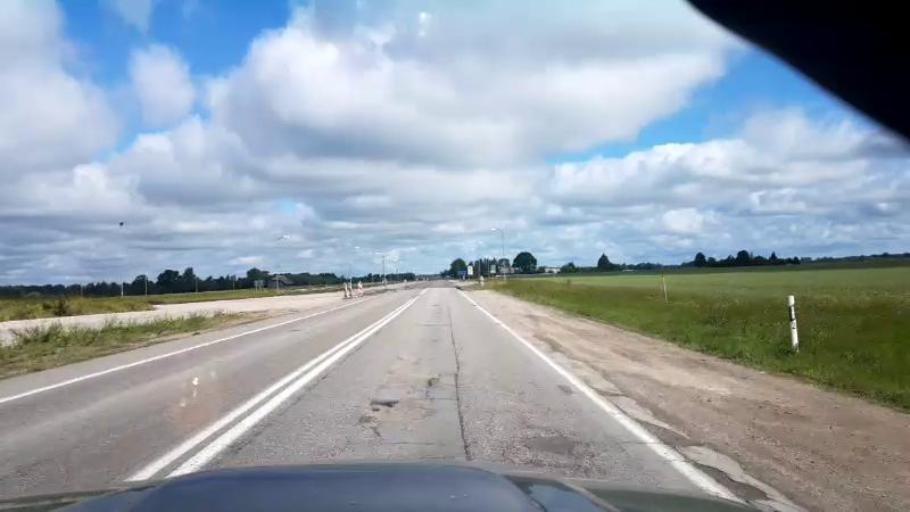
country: LV
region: Bauskas Rajons
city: Bauska
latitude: 56.2799
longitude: 24.3620
